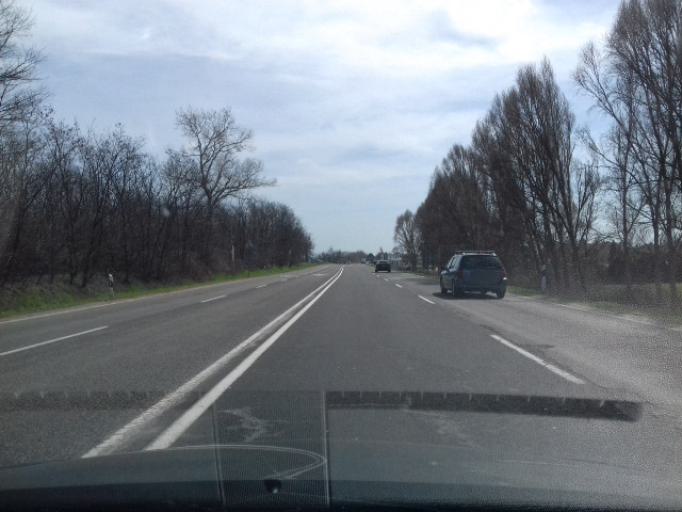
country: HU
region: Bacs-Kiskun
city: Kecskemet
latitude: 46.9630
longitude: 19.6419
